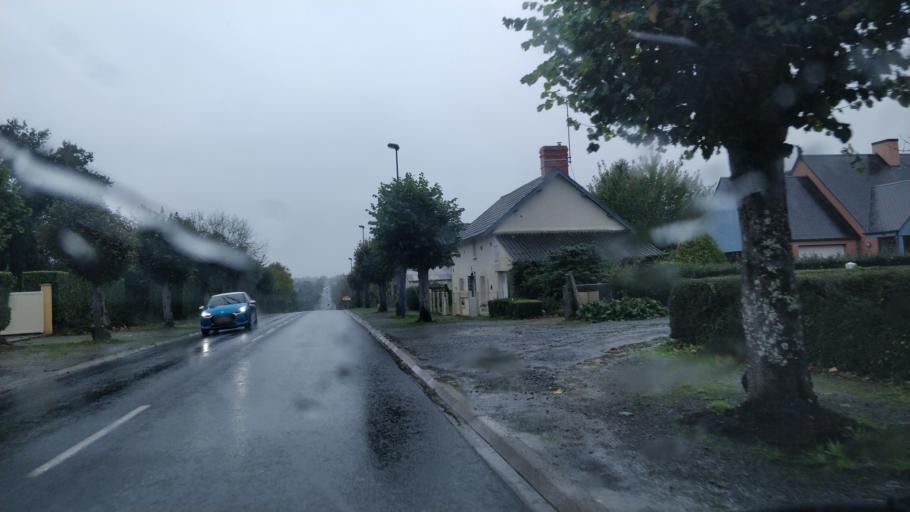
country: FR
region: Lower Normandy
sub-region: Departement de la Manche
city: Brehal
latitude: 48.8924
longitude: -1.5172
